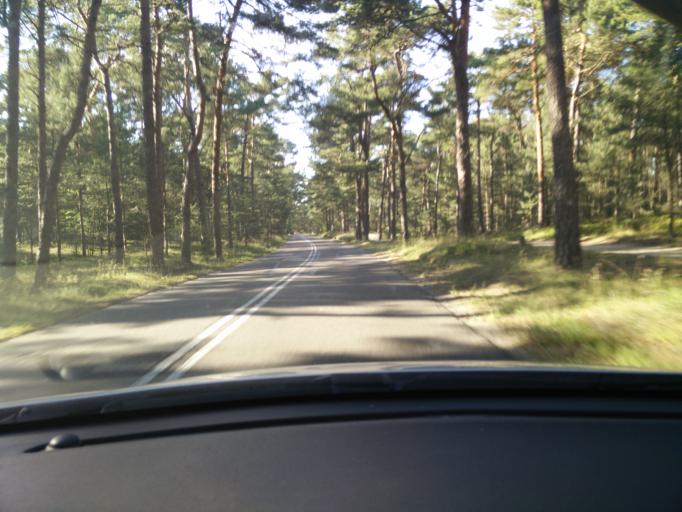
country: PL
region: Pomeranian Voivodeship
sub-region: Powiat pucki
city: Jastarnia
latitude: 54.6629
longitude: 18.7465
